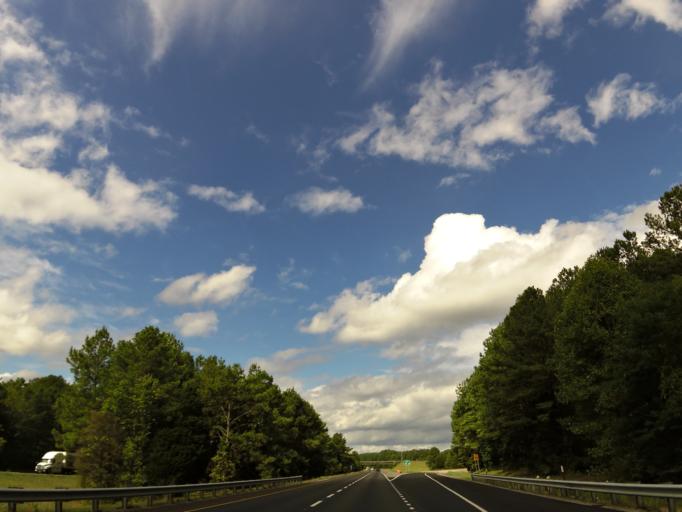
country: US
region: Tennessee
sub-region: Bradley County
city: Hopewell
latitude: 35.3259
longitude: -84.7771
